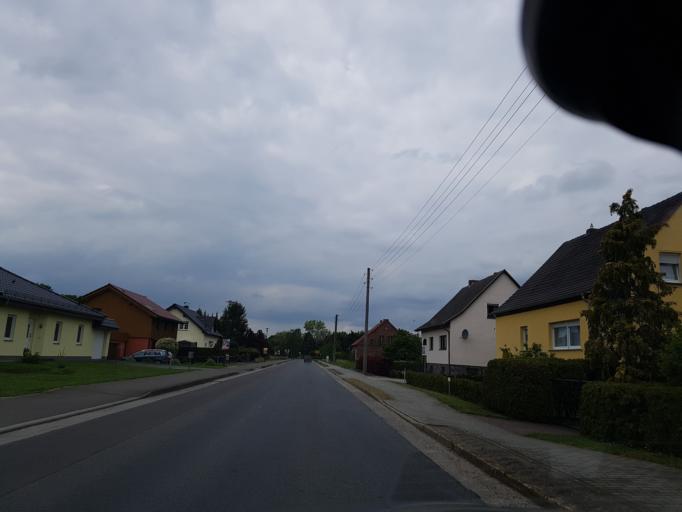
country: DE
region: Brandenburg
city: Luckau
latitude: 51.8533
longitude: 13.7422
